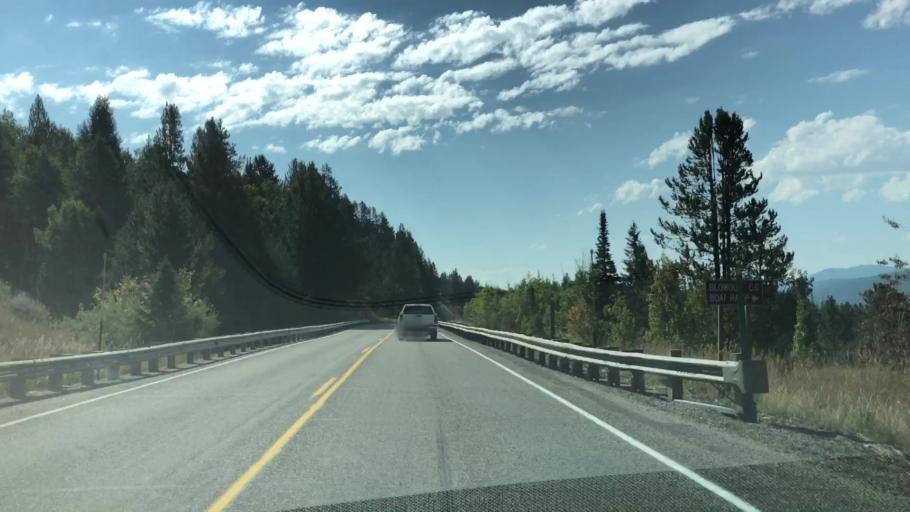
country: US
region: Idaho
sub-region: Teton County
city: Victor
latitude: 43.2897
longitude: -111.1228
